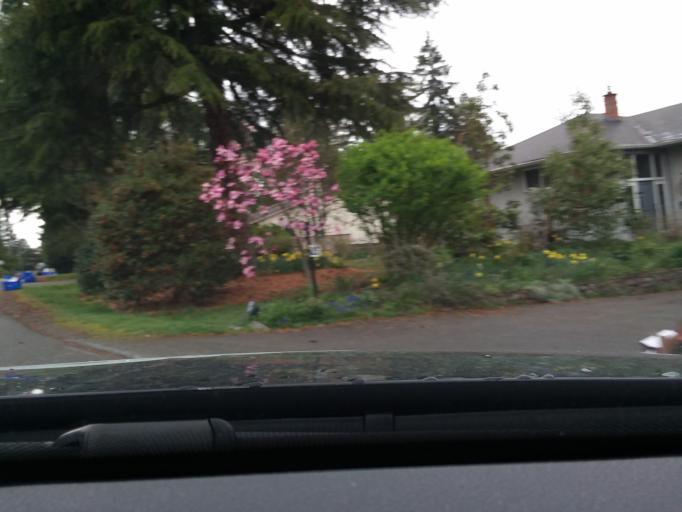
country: CA
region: British Columbia
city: North Saanich
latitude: 48.5521
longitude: -123.3971
